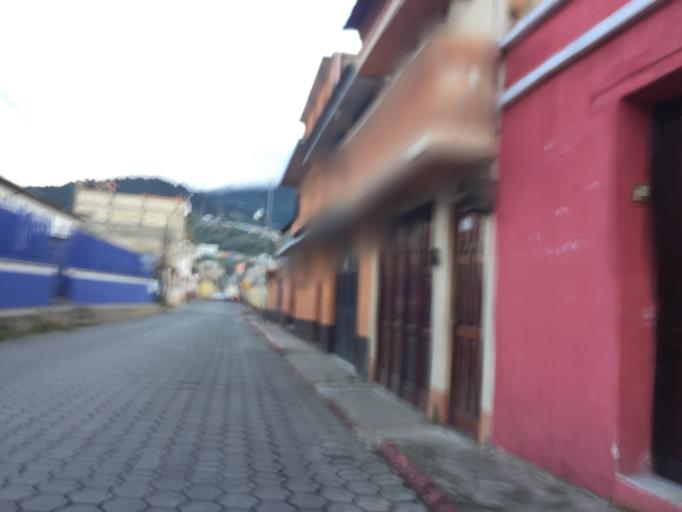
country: GT
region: Totonicapan
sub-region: Municipio de Totonicapan
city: Totonicapan
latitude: 14.9134
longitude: -91.3625
